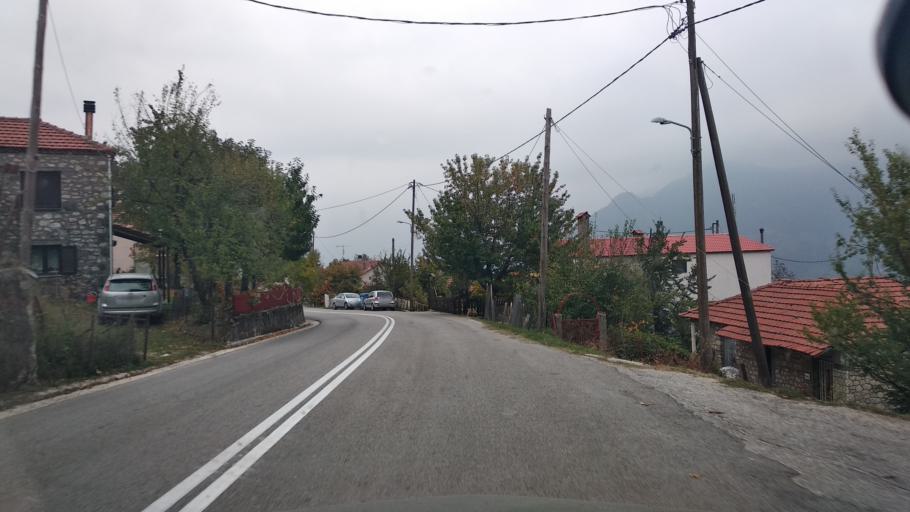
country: GR
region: Thessaly
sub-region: Trikala
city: Pyli
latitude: 39.5056
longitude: 21.5350
